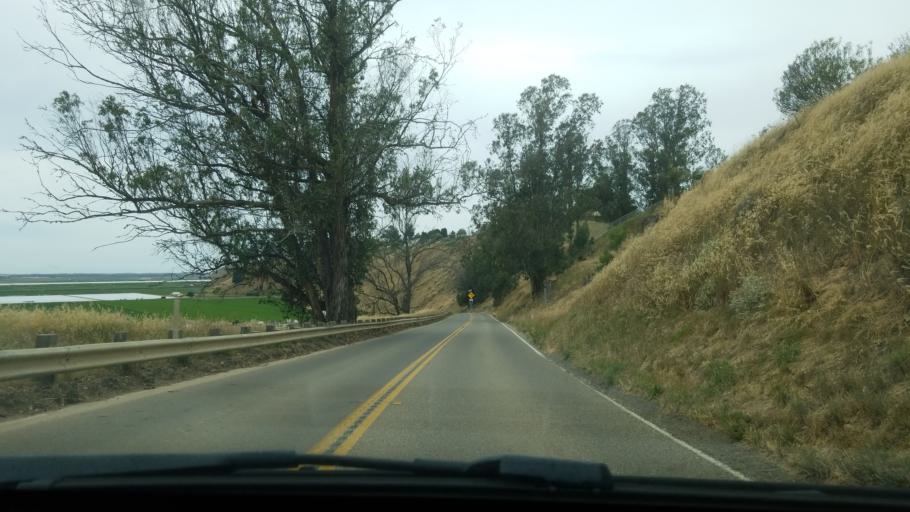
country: US
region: California
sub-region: San Luis Obispo County
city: Nipomo
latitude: 35.0091
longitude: -120.4981
